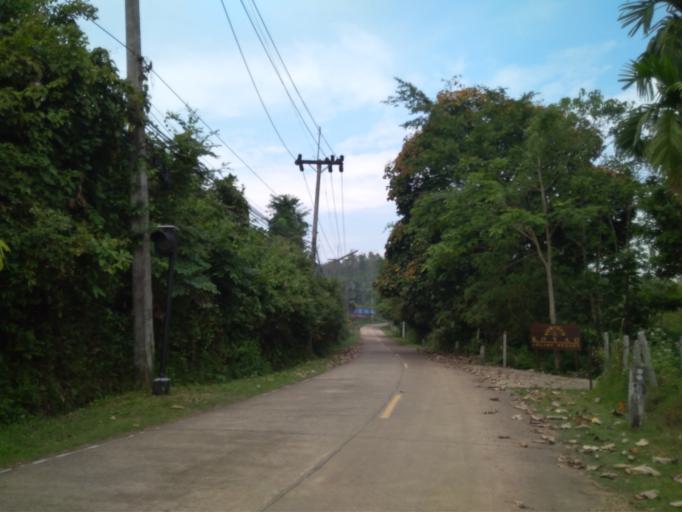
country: TH
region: Phangnga
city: Ko Yao
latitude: 8.1171
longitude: 98.6231
